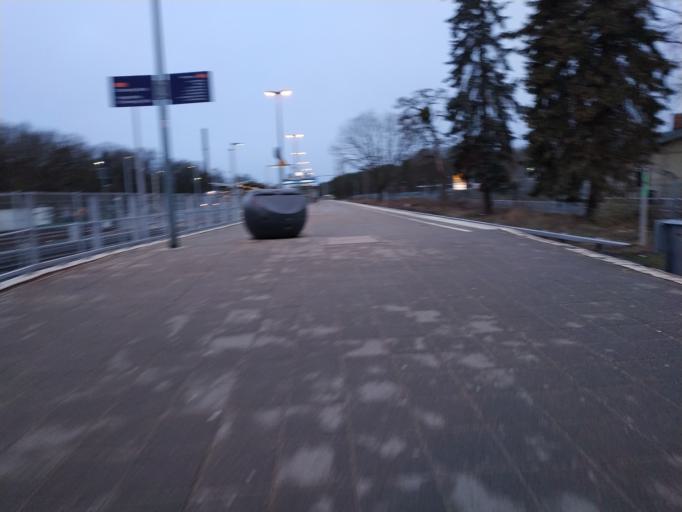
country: DE
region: Brandenburg
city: Petershagen
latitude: 52.5322
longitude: 13.8349
